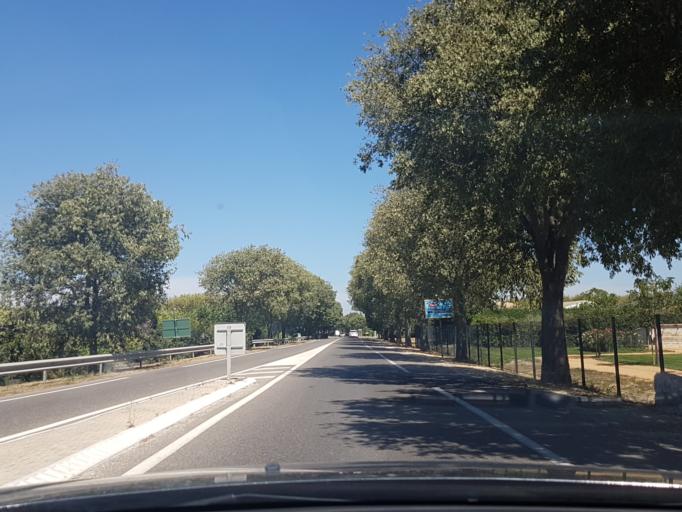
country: FR
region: Provence-Alpes-Cote d'Azur
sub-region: Departement des Bouches-du-Rhone
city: Eyragues
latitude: 43.8416
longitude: 4.8377
